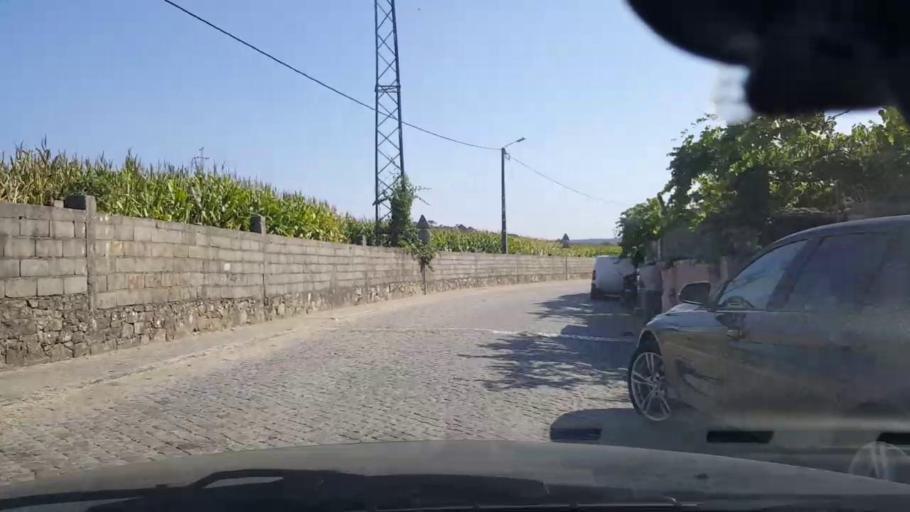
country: PT
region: Porto
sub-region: Povoa de Varzim
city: Pedroso
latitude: 41.4101
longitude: -8.6942
